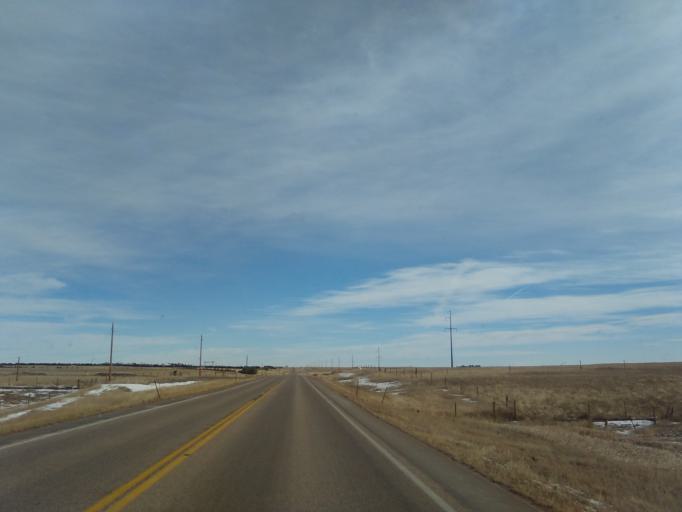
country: US
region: Wyoming
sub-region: Laramie County
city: Ranchettes
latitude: 41.4148
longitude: -104.4229
